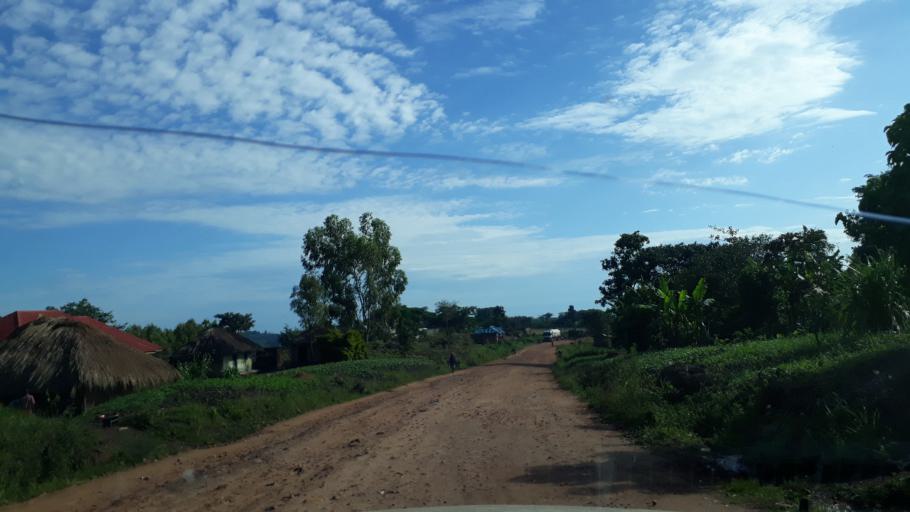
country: UG
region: Northern Region
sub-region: Zombo District
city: Paidha
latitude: 2.3039
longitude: 31.0156
